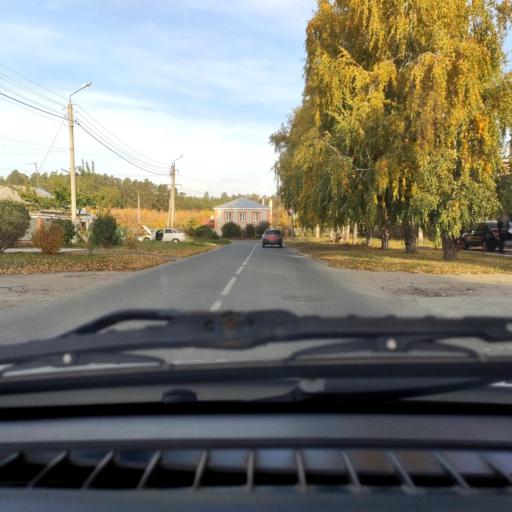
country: RU
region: Samara
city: Tol'yatti
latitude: 53.5187
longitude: 49.3973
